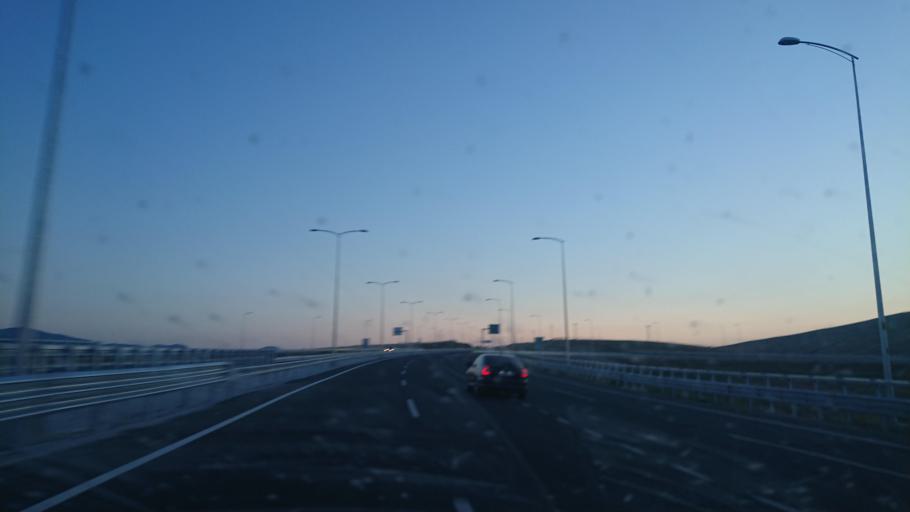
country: TR
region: Aksaray
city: Balci
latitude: 38.7726
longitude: 34.1067
